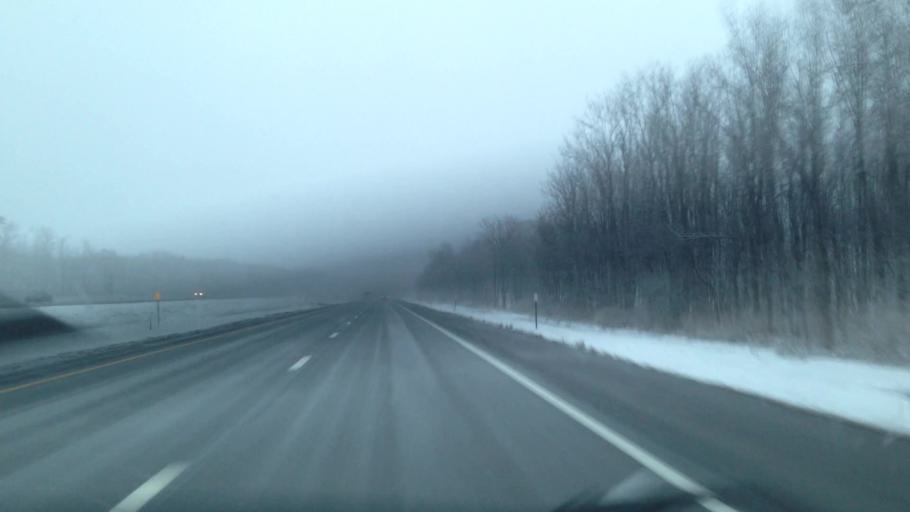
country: US
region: New York
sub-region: Madison County
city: Canastota
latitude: 43.0939
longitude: -75.8107
